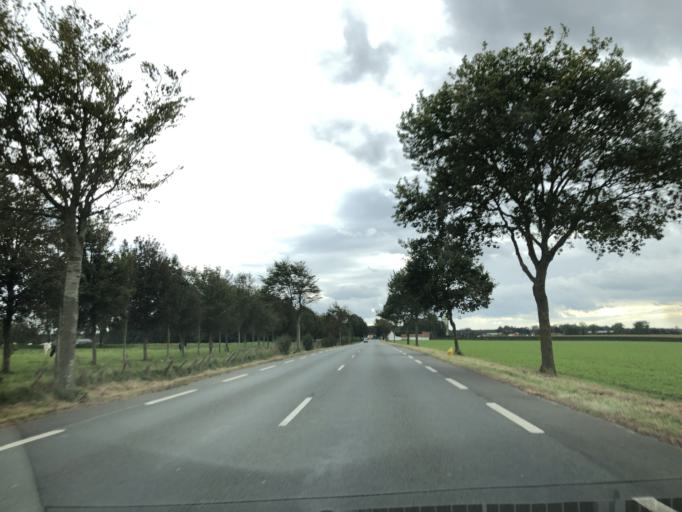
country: FR
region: Nord-Pas-de-Calais
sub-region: Departement du Pas-de-Calais
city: Hesdin
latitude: 50.4186
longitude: 2.0531
